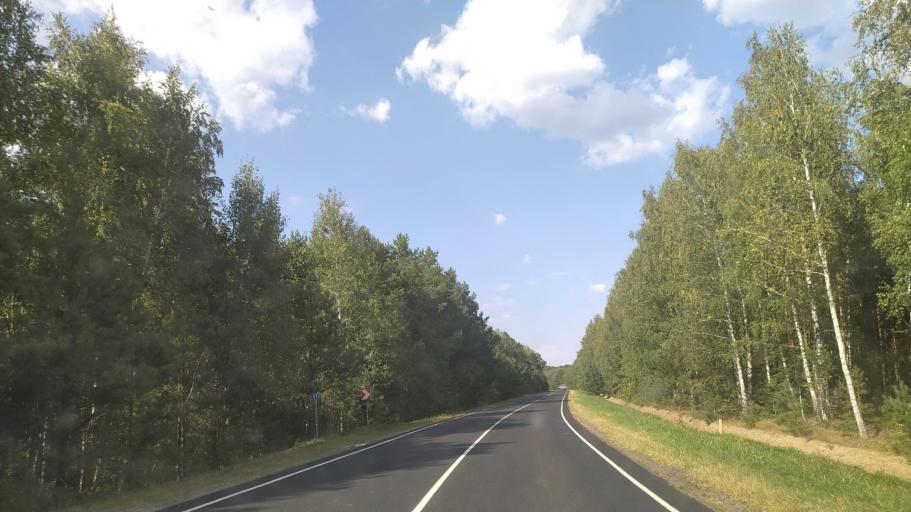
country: BY
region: Brest
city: Drahichyn
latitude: 52.2707
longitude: 25.0707
